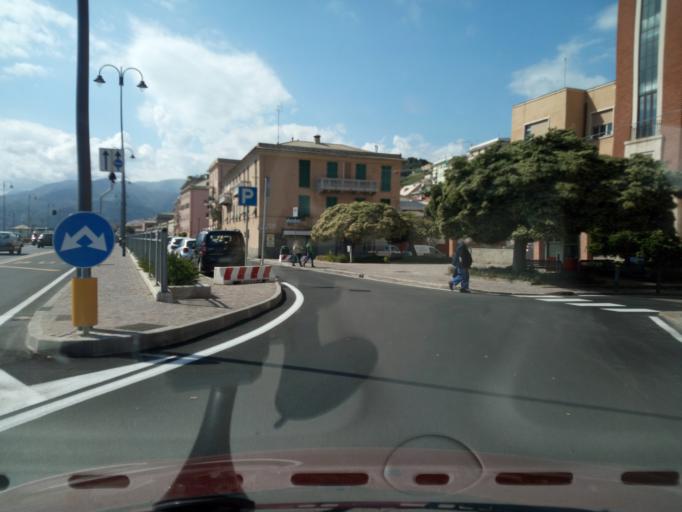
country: IT
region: Liguria
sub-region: Provincia di Genova
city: Mele
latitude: 44.4264
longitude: 8.7901
